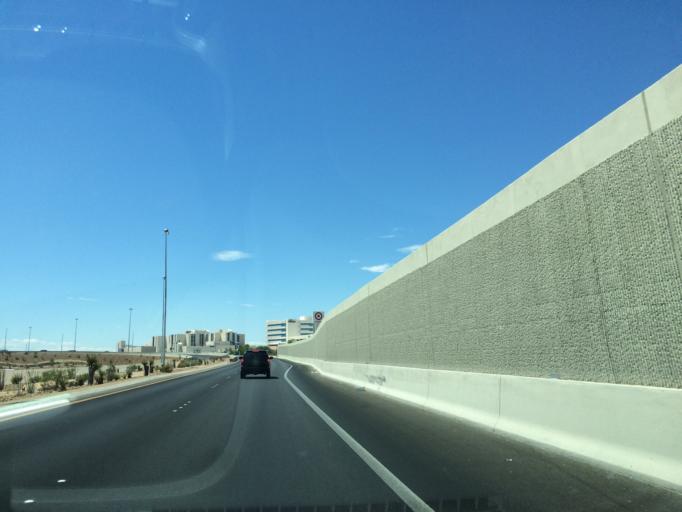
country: US
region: Nevada
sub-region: Clark County
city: Spring Valley
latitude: 36.2210
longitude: -115.2476
